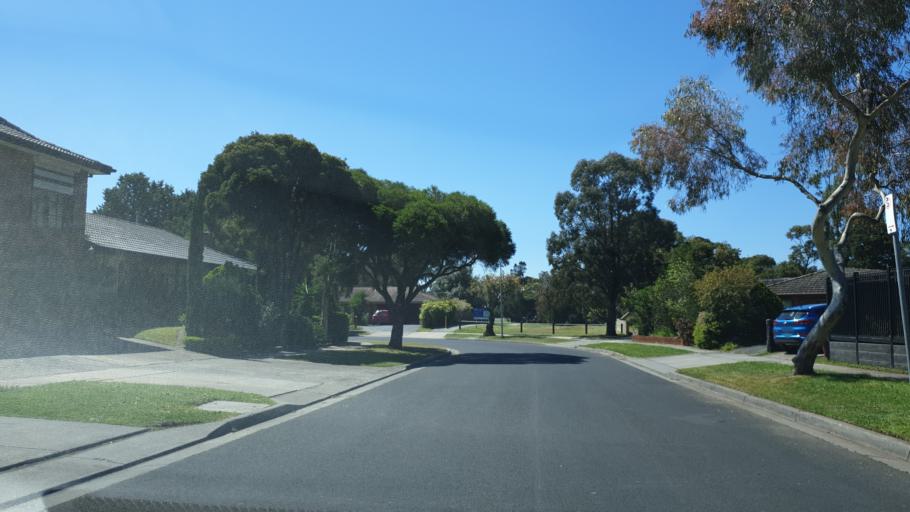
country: AU
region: Victoria
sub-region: Casey
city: Cranbourne North
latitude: -38.0871
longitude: 145.2772
